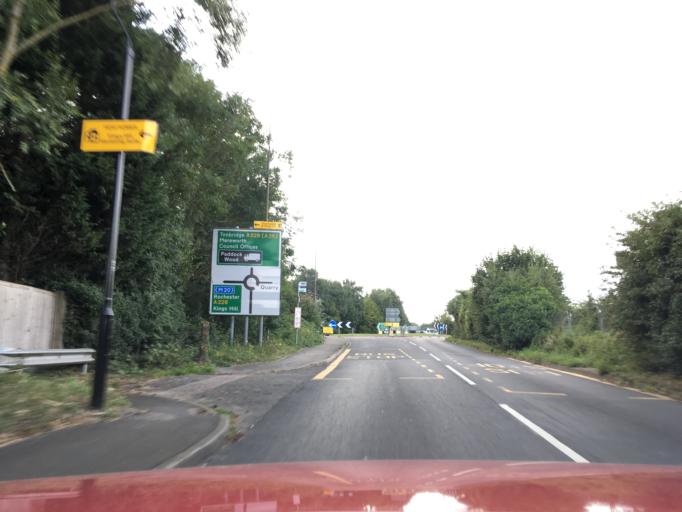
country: GB
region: England
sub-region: Kent
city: Kings Hill
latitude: 51.2807
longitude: 0.3954
